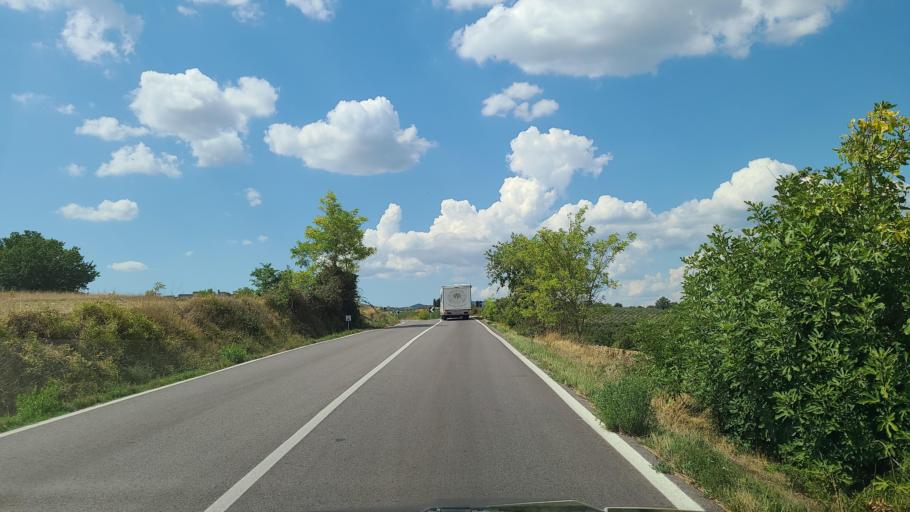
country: IT
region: Tuscany
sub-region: Provincia di Siena
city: Casole d'Elsa
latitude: 43.4029
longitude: 11.0349
